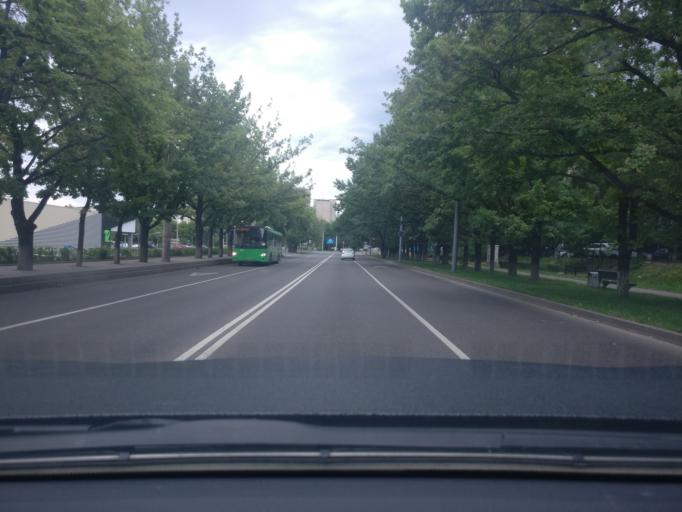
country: KZ
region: Almaty Qalasy
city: Almaty
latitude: 43.2379
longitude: 76.8572
